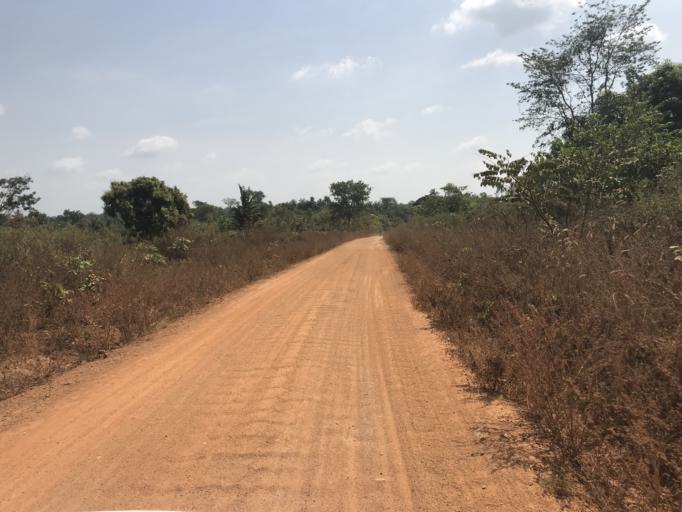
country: NG
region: Osun
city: Ifon
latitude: 7.9216
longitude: 4.4825
